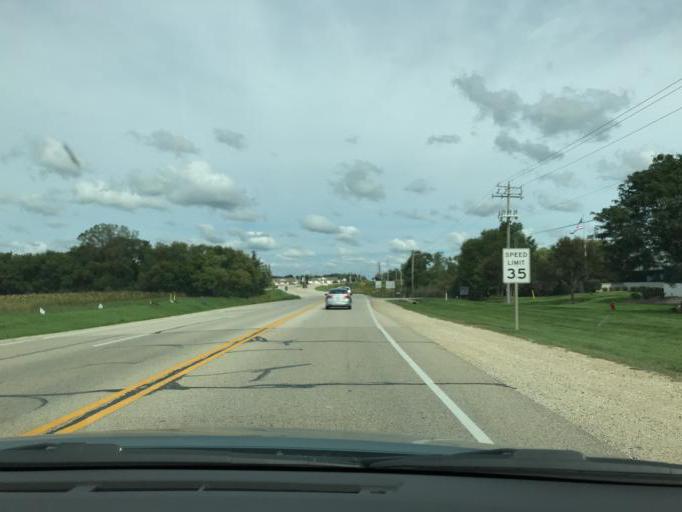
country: US
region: Wisconsin
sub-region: Racine County
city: Burlington
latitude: 42.6544
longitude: -88.2582
